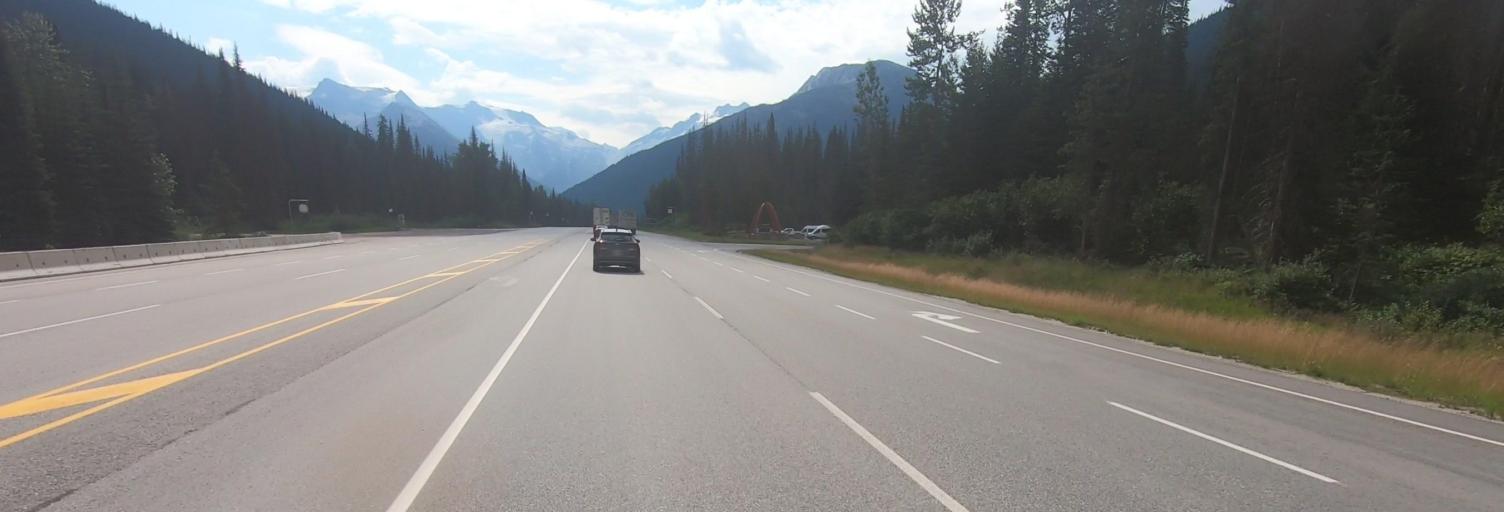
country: CA
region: British Columbia
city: Golden
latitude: 51.2910
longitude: -117.5157
